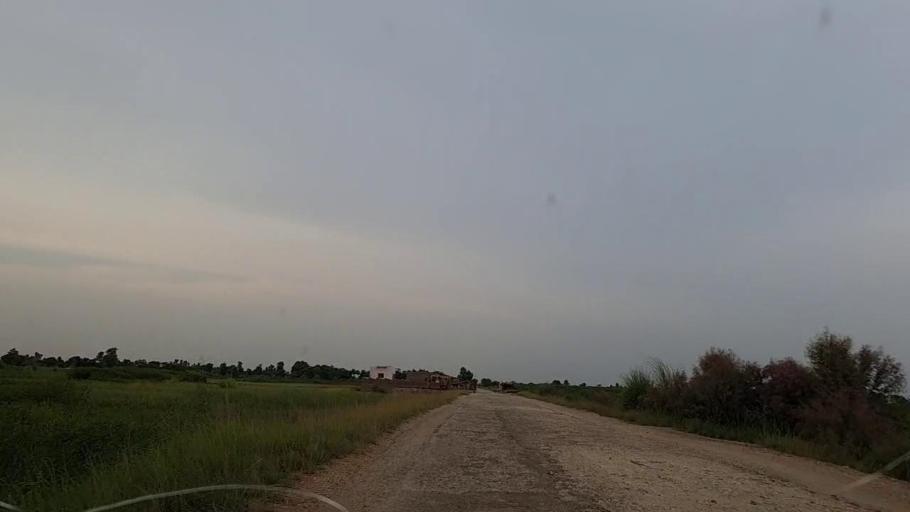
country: PK
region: Sindh
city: Mirpur Mathelo
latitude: 27.8790
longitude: 69.6371
